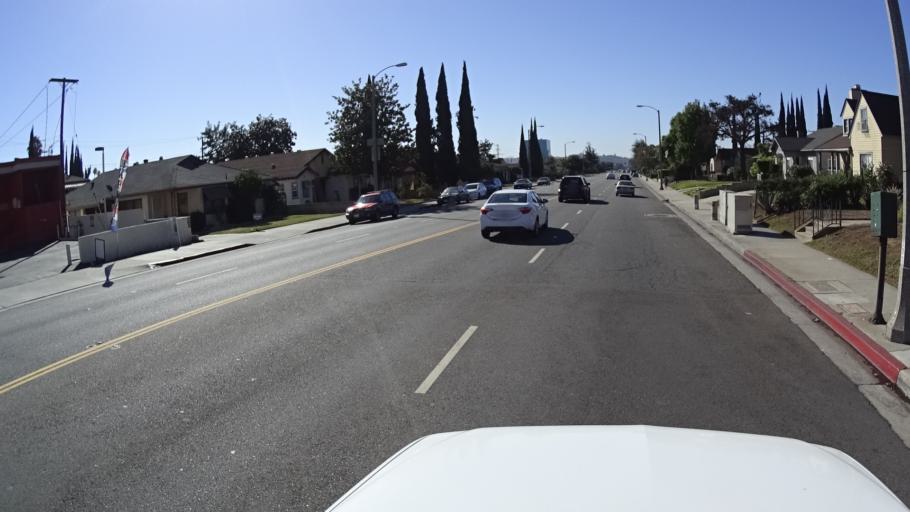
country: US
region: California
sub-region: Los Angeles County
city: South Pasadena
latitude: 34.0946
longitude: -118.1522
